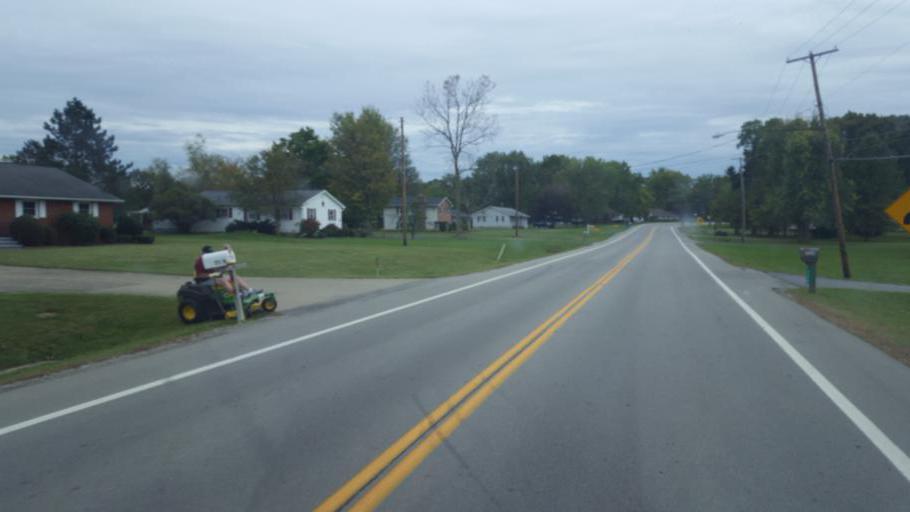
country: US
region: Ohio
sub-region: Huron County
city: Wakeman
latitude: 41.3280
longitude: -82.3609
